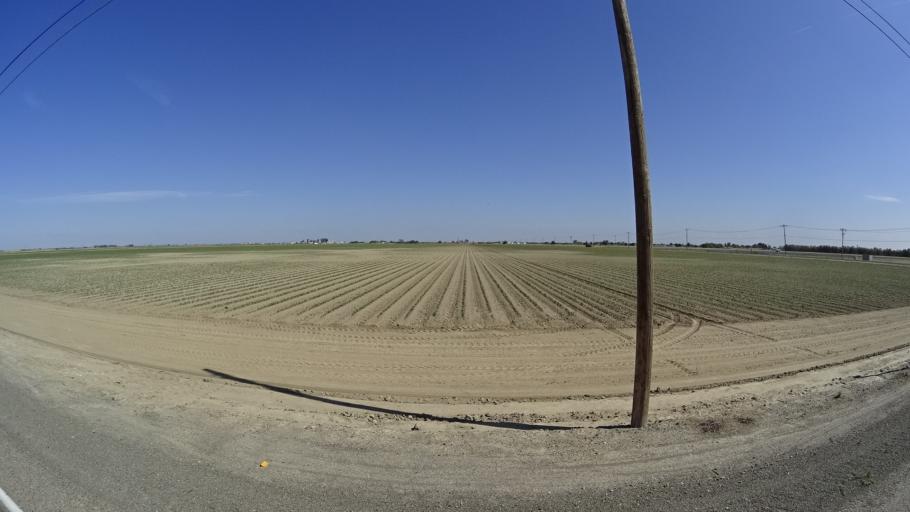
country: US
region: California
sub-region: Kings County
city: Lemoore
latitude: 36.2547
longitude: -119.8001
